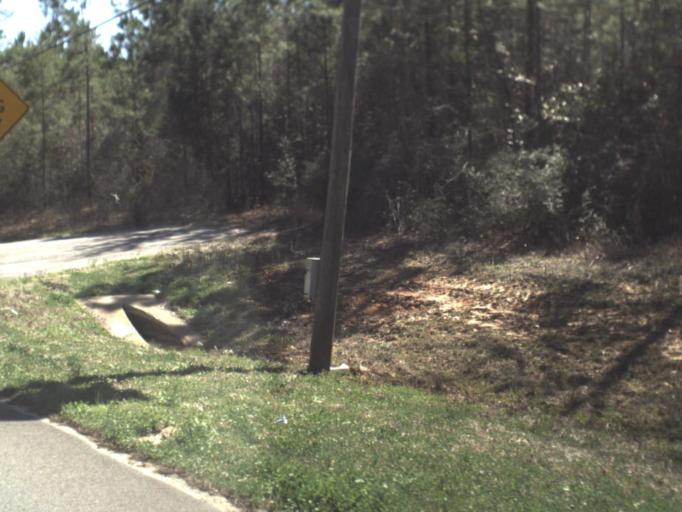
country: US
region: Florida
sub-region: Jackson County
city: Marianna
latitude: 30.7925
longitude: -85.2655
